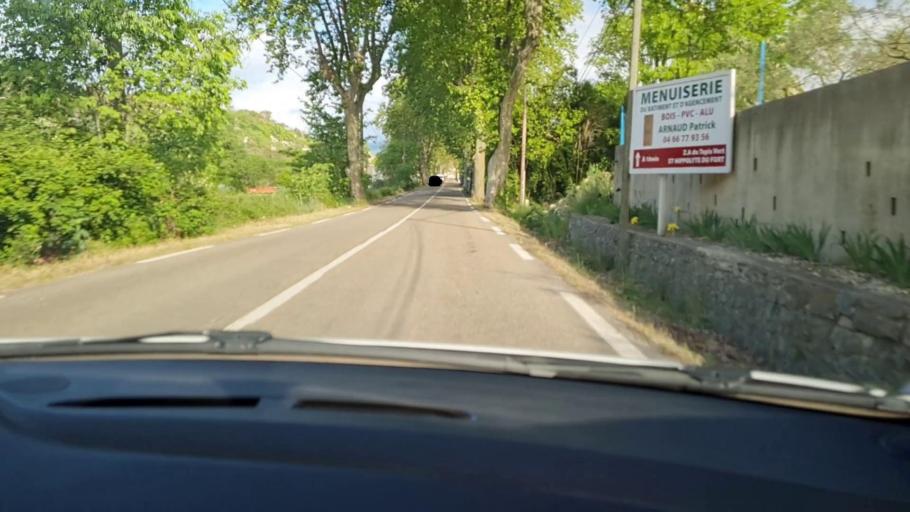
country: FR
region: Languedoc-Roussillon
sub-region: Departement du Gard
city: Sauve
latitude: 43.9371
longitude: 3.9590
